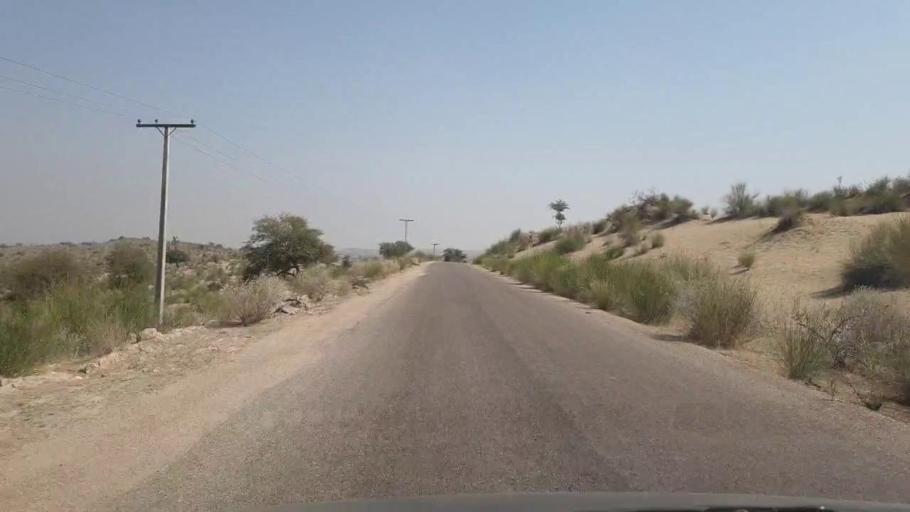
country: PK
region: Sindh
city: Chor
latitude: 25.6713
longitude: 70.1447
